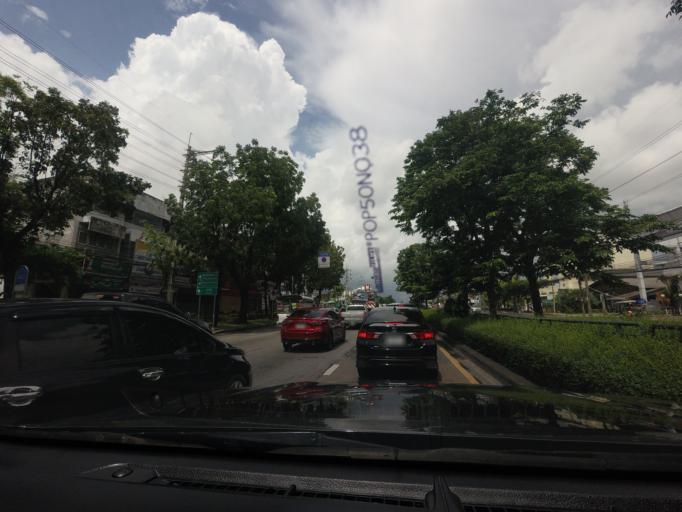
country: TH
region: Bangkok
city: Nong Khaem
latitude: 13.7080
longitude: 100.3750
